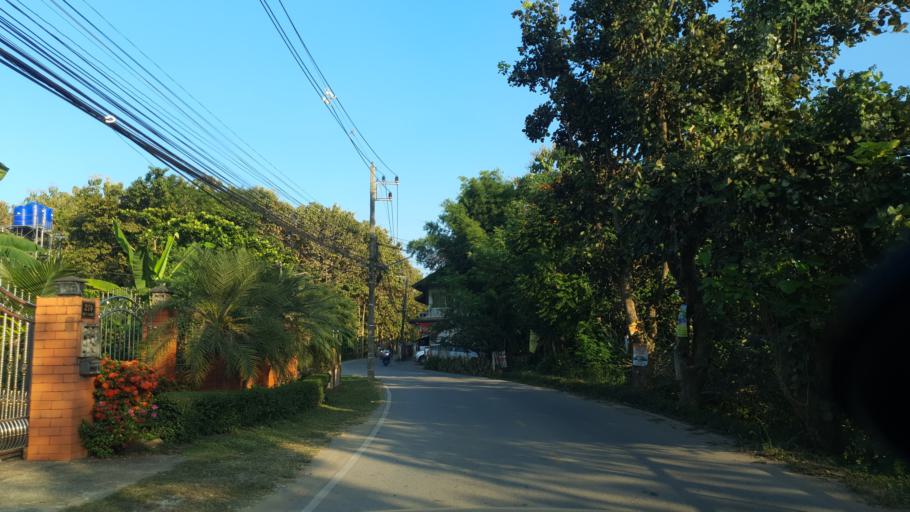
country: TH
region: Chiang Mai
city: San Sai
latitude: 18.9045
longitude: 98.9437
